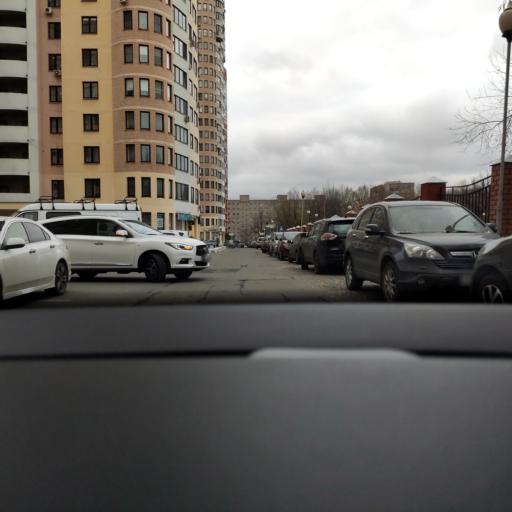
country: RU
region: Moskovskaya
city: Reutov
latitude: 55.7530
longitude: 37.8677
